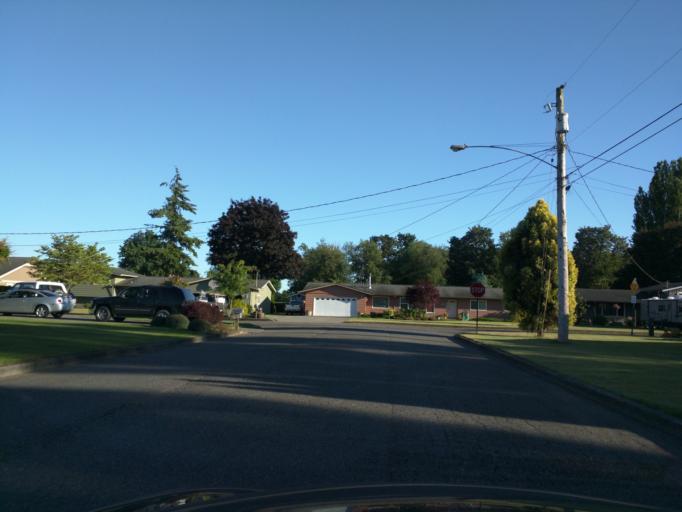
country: US
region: Washington
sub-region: Whatcom County
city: Lynden
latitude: 48.9448
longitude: -122.4837
